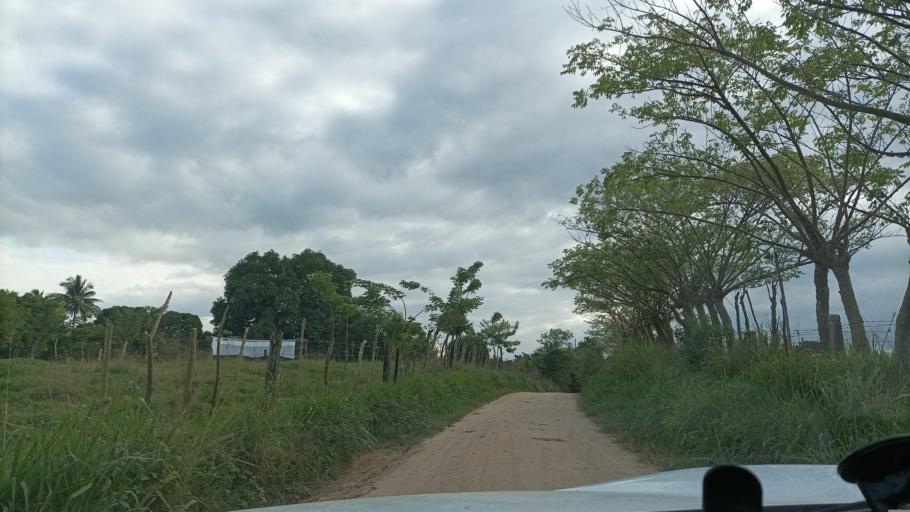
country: MX
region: Veracruz
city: Oluta
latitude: 17.9278
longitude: -94.8838
